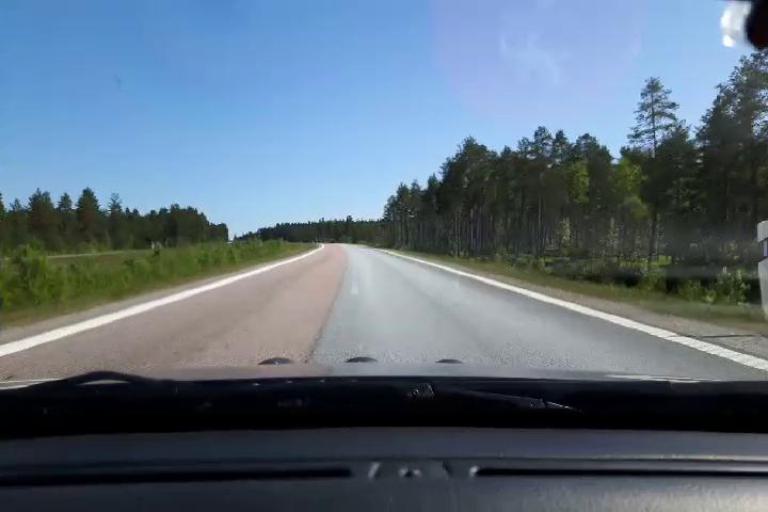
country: SE
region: Gaevleborg
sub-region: Soderhamns Kommun
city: Soderhamn
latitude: 61.3782
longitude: 16.9947
